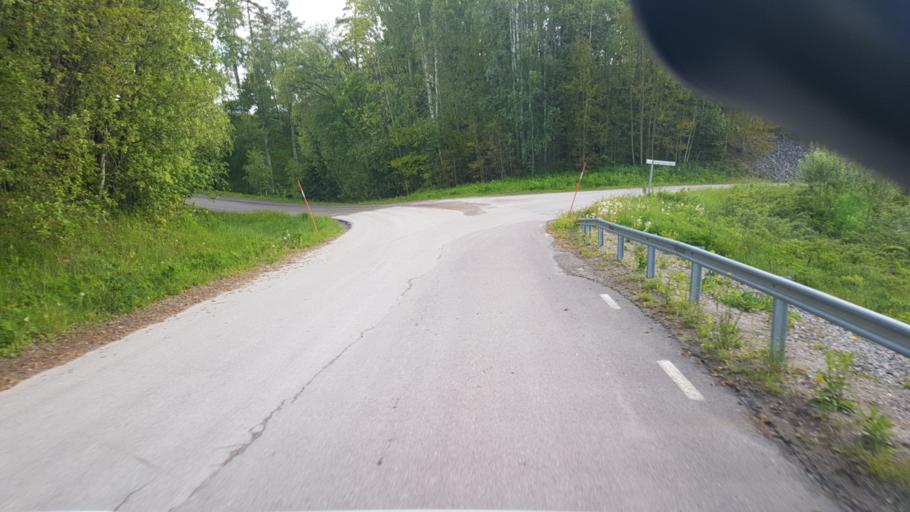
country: SE
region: Vaermland
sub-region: Eda Kommun
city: Amotfors
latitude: 59.7138
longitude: 12.1484
